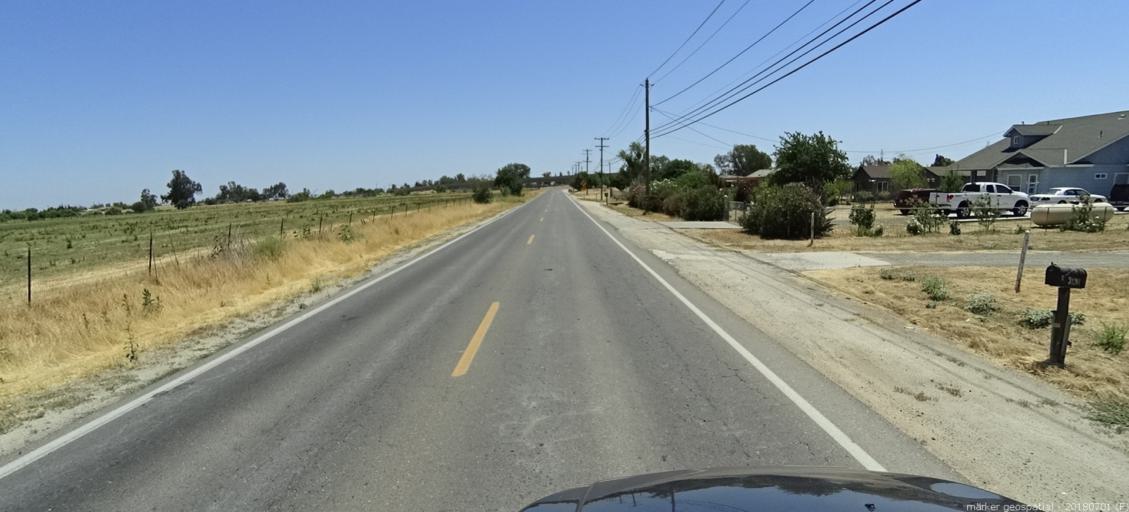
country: US
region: California
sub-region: Madera County
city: Parksdale
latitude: 36.9883
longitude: -120.0287
